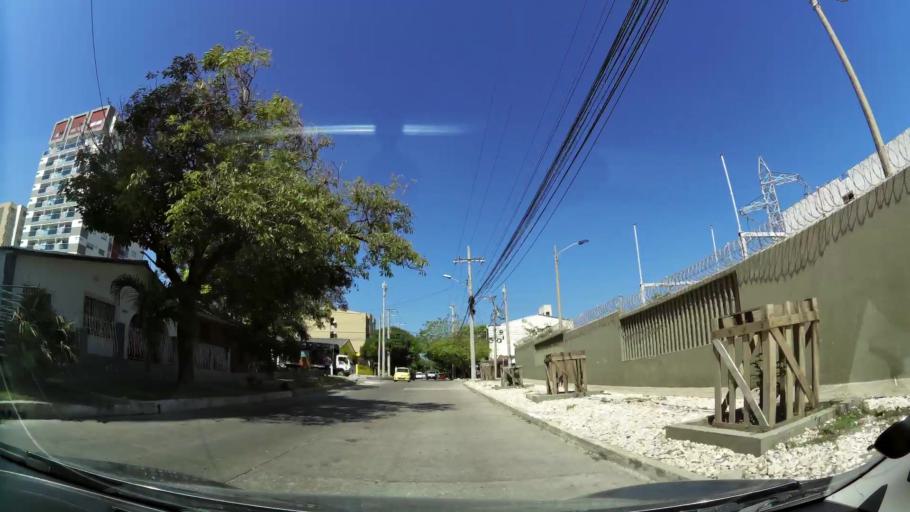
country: CO
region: Atlantico
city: Barranquilla
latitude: 11.0088
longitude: -74.7957
